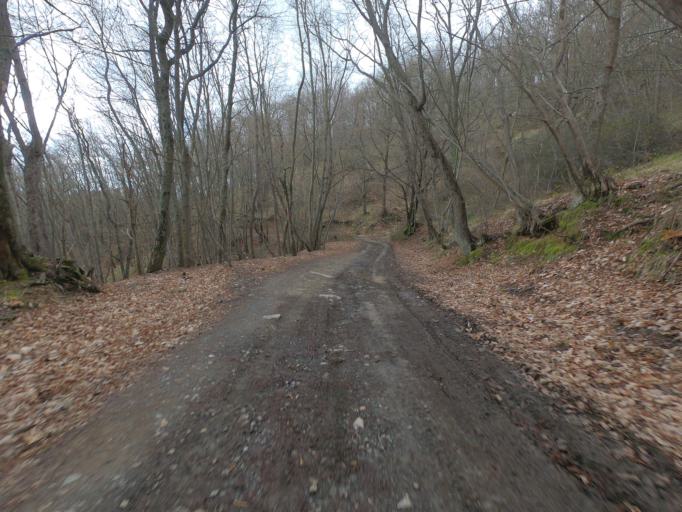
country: IT
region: Liguria
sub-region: Provincia di Imperia
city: Pietrabruna
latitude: 43.9120
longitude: 7.8909
